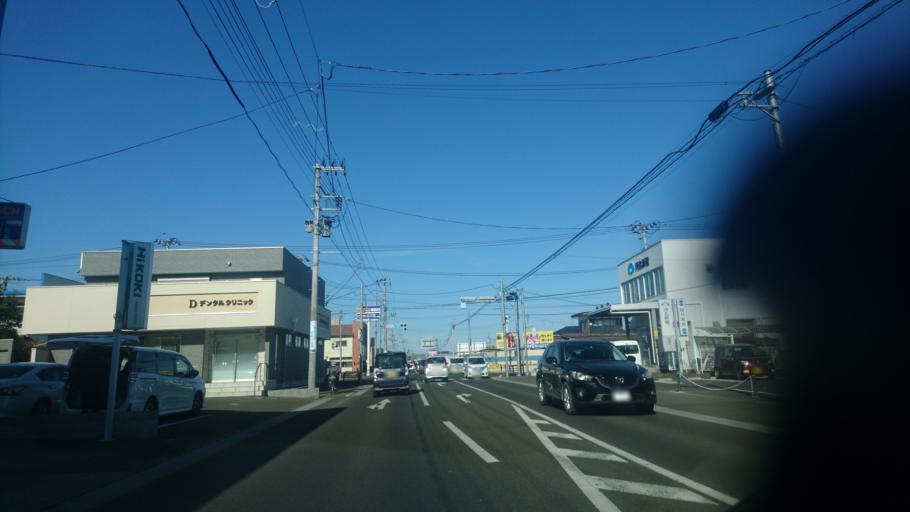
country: JP
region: Miyagi
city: Iwanuma
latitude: 38.1793
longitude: 140.8857
